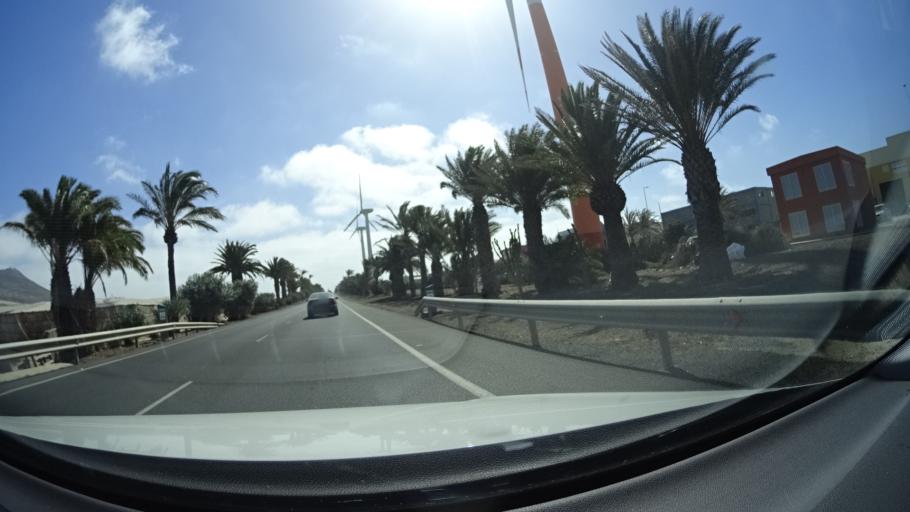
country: ES
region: Canary Islands
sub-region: Provincia de Las Palmas
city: Cruce de Arinaga
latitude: 27.8649
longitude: -15.4092
